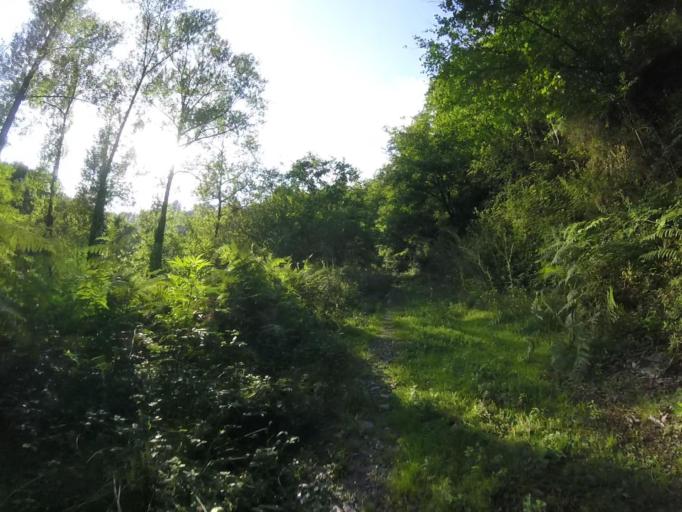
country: ES
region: Navarre
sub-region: Provincia de Navarra
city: Arano
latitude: 43.2269
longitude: -1.9093
